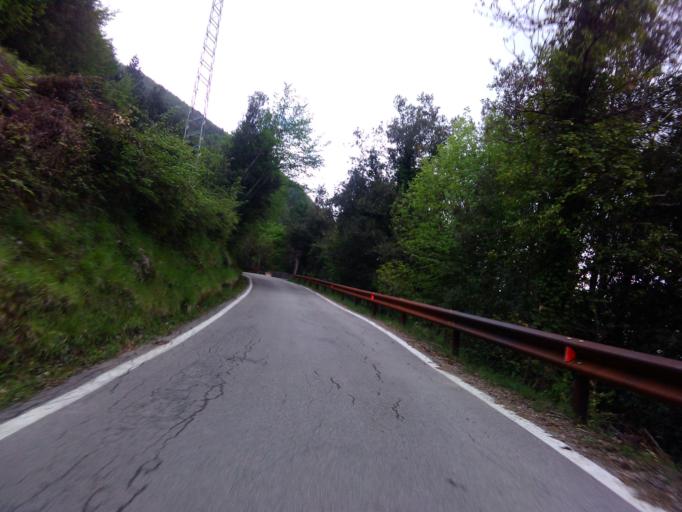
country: IT
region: Tuscany
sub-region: Provincia di Lucca
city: Pontestazzemese
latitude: 43.9680
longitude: 10.2811
